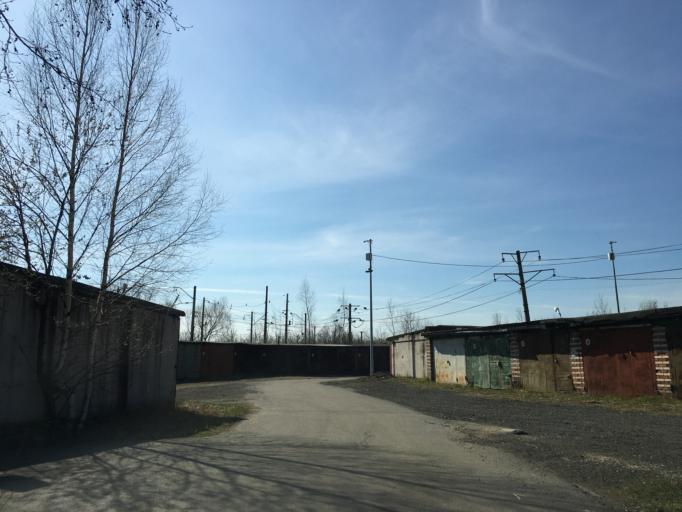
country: RU
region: St.-Petersburg
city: Uritsk
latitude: 59.8192
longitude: 30.1642
